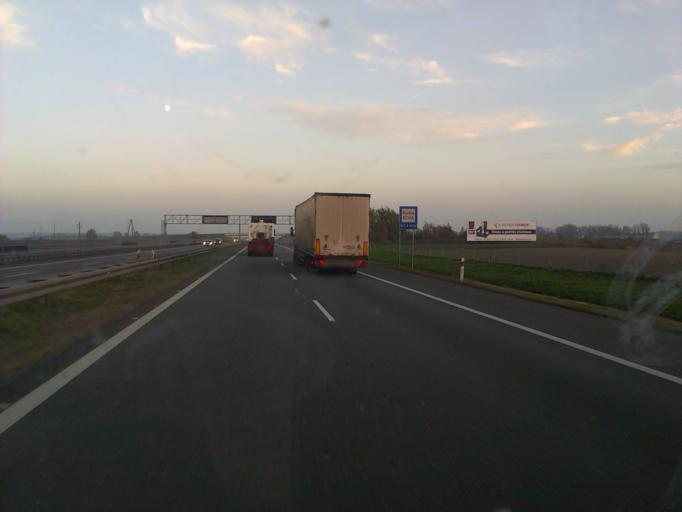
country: PL
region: Opole Voivodeship
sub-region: Powiat krapkowicki
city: Krapkowice
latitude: 50.5260
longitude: 17.9273
